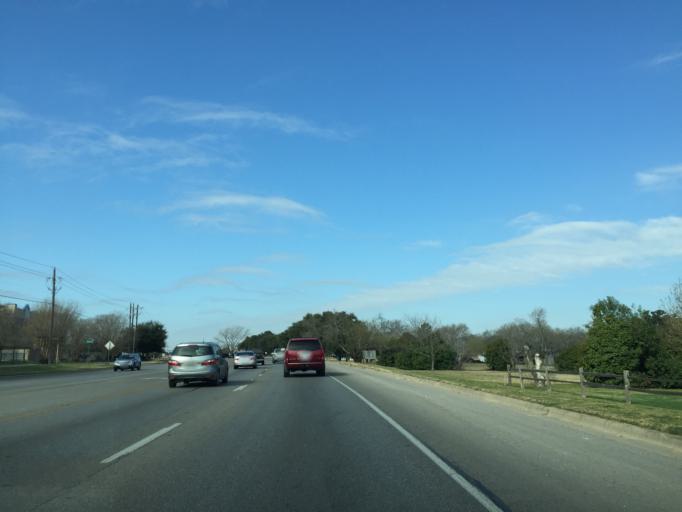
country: US
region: Texas
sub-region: Williamson County
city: Round Rock
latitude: 30.5190
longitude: -97.6752
